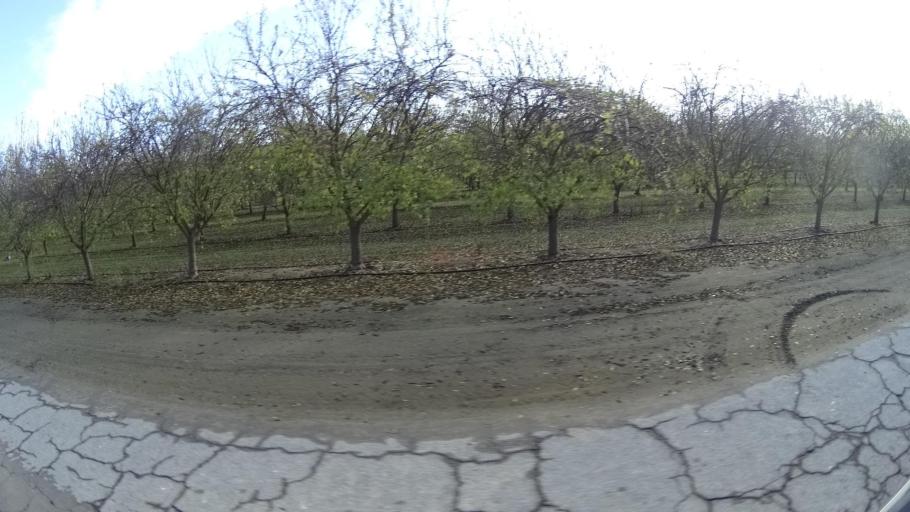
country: US
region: California
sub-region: Kern County
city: Delano
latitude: 35.7151
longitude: -119.3208
